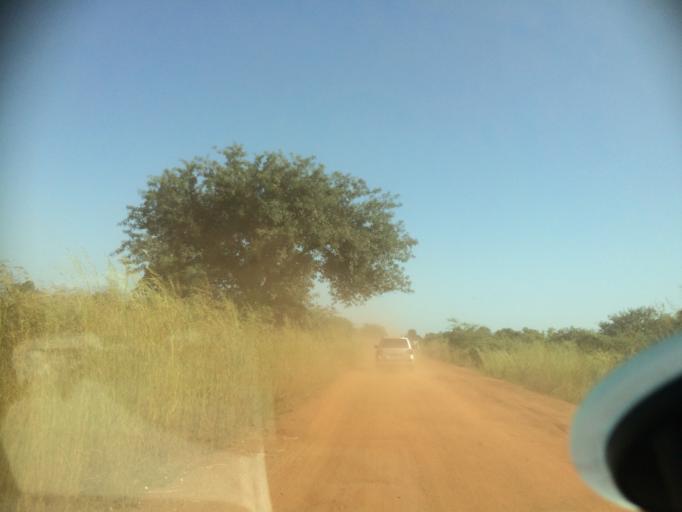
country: SS
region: Central Equatoria
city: Juba
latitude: 4.9844
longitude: 31.8680
